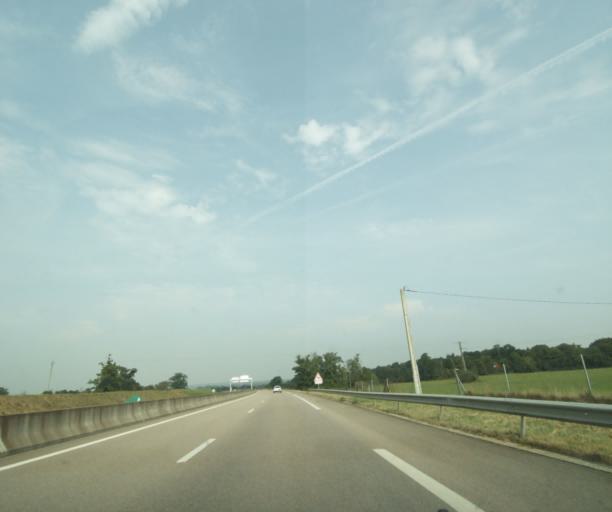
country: FR
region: Lower Normandy
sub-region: Departement du Calvados
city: Falaise
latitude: 48.8561
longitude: -0.1802
